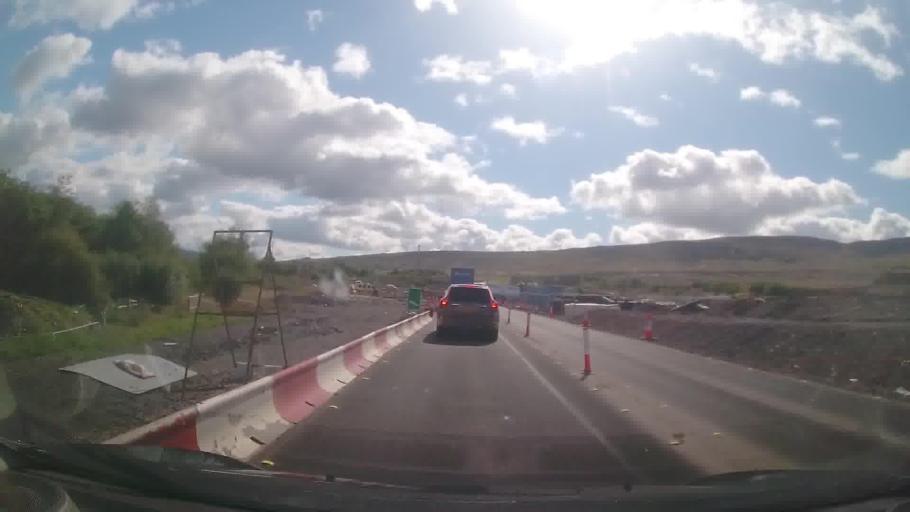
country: GB
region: Wales
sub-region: Rhondda Cynon Taf
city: Hirwaun
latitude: 51.7392
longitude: -3.5242
